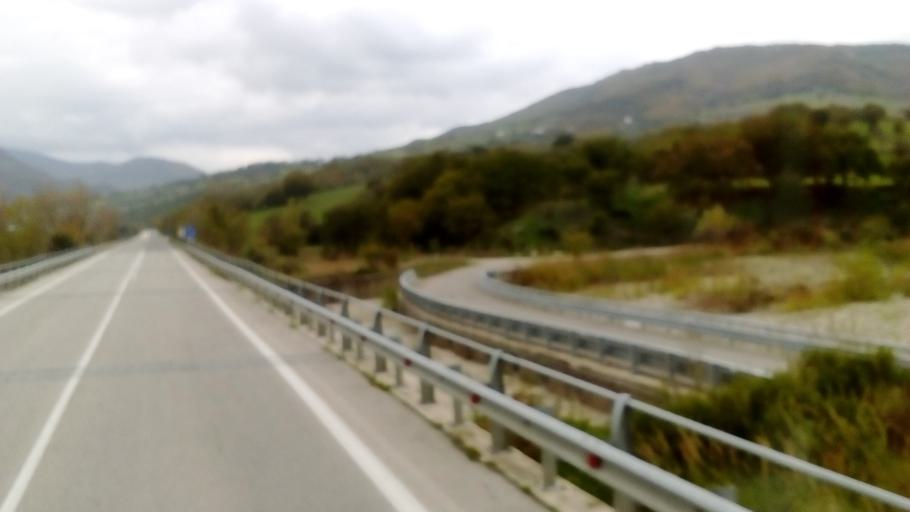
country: IT
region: Abruzzo
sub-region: Provincia di Chieti
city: San Giovanni Lipioni
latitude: 41.8256
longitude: 14.5722
